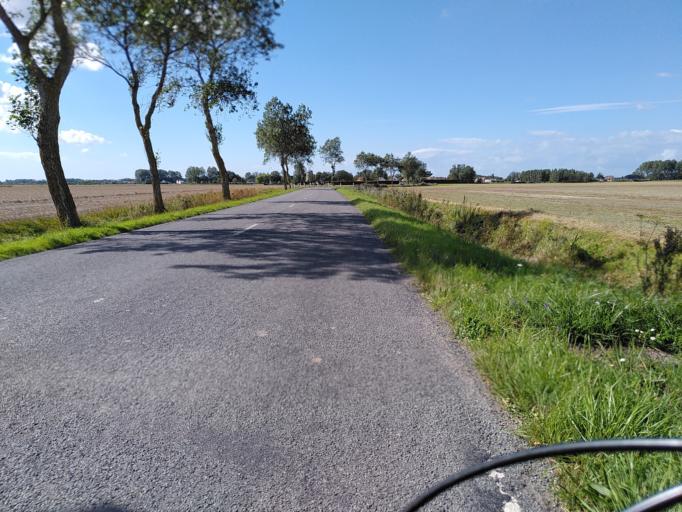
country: FR
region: Nord-Pas-de-Calais
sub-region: Departement du Nord
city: Grand-Fort-Philippe
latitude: 50.9897
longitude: 2.1043
